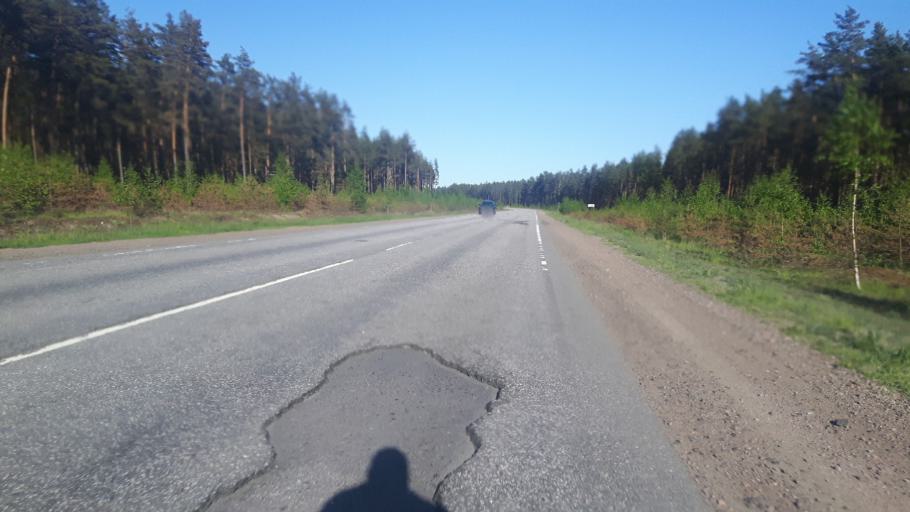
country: RU
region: Leningrad
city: Lebyazh'ye
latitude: 60.1678
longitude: 29.2431
